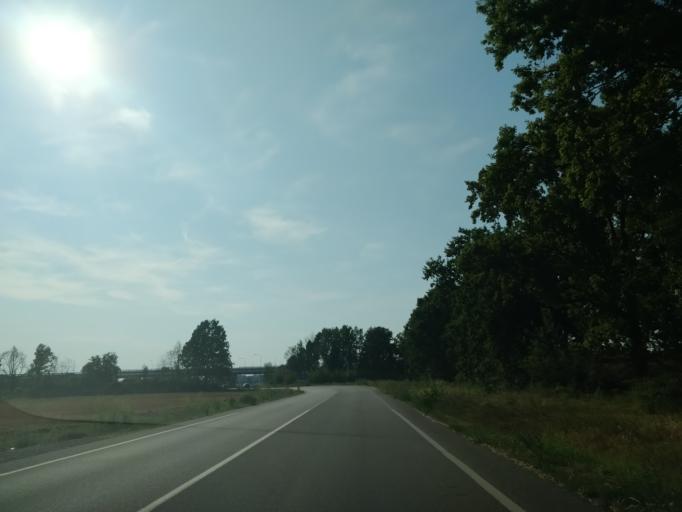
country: IT
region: Emilia-Romagna
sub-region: Provincia di Bologna
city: Progresso
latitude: 44.5617
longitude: 11.3473
